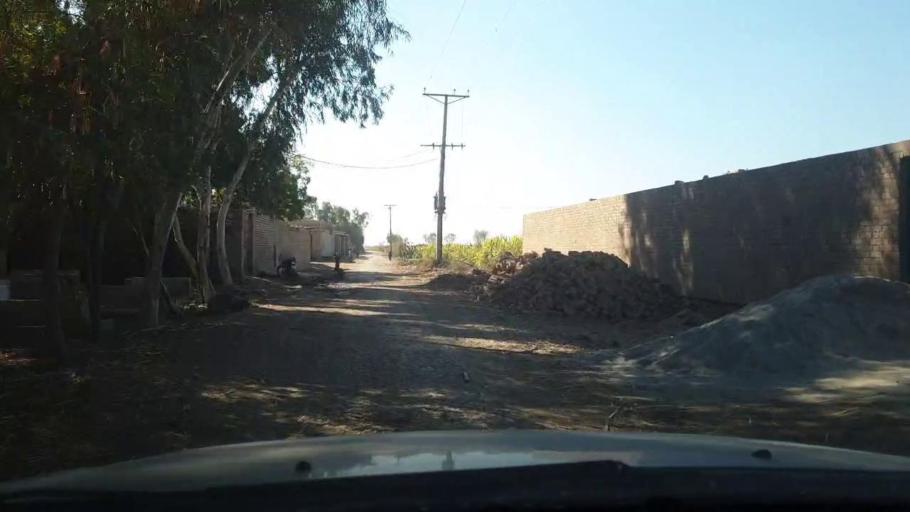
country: PK
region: Sindh
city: Ghotki
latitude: 27.9850
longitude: 69.2224
